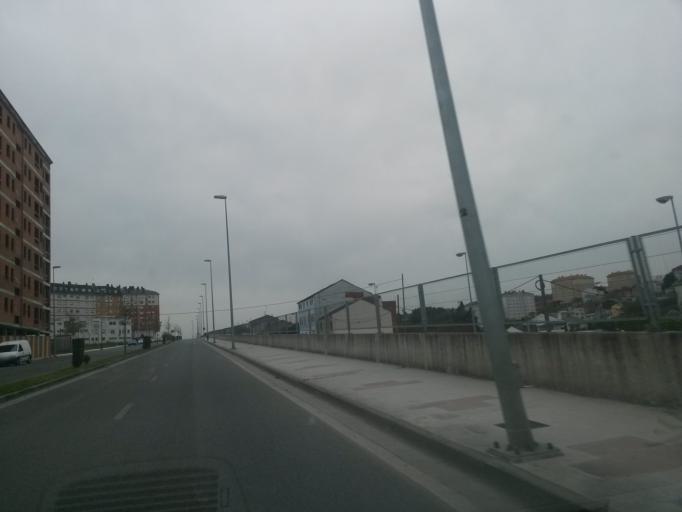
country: ES
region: Galicia
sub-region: Provincia de Lugo
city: Lugo
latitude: 43.0199
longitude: -7.5571
